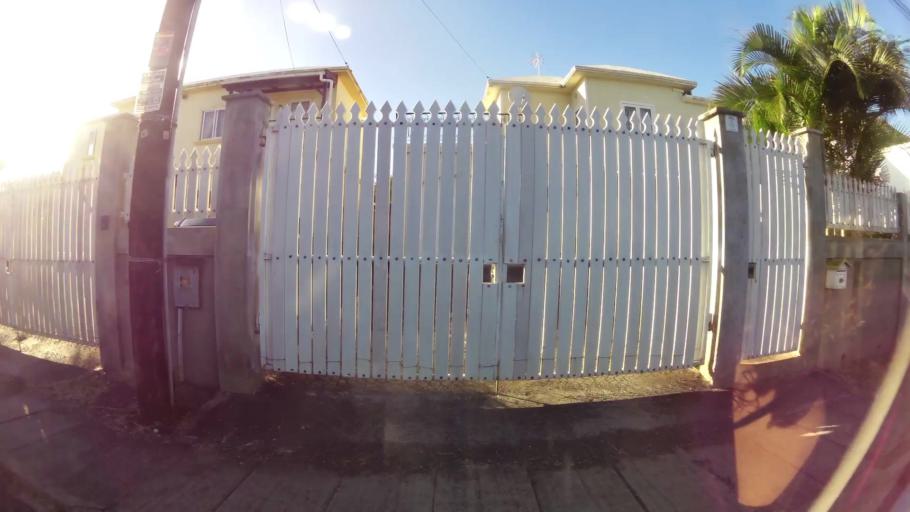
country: MU
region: Black River
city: Tamarin
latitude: -20.3352
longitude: 57.3712
